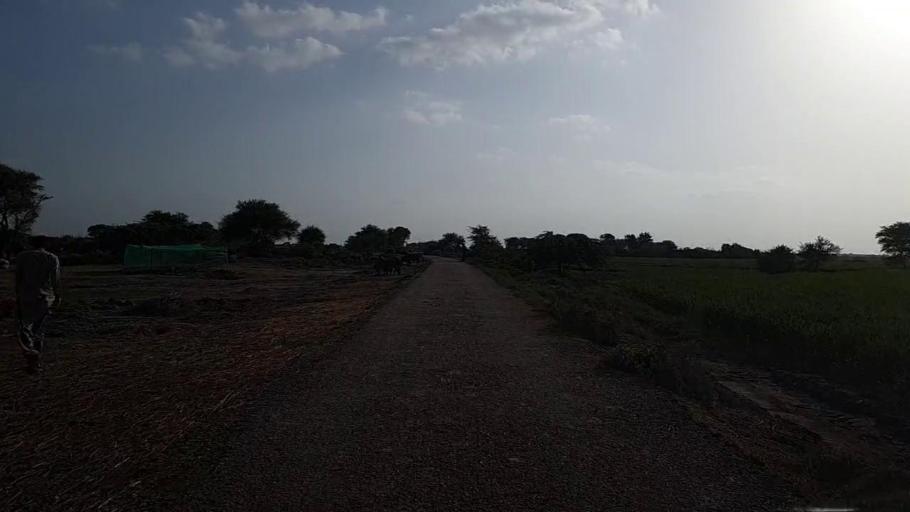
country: PK
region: Sindh
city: Kario
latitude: 24.6699
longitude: 68.4560
